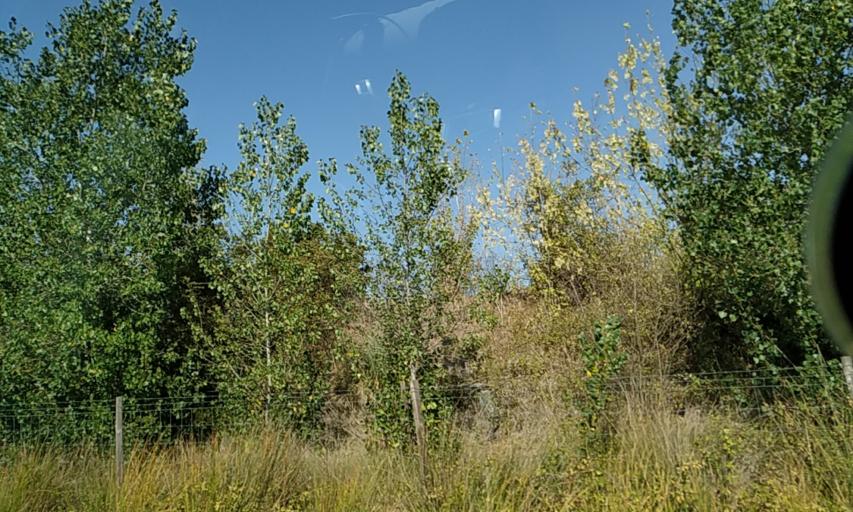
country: PT
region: Santarem
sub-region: Coruche
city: Coruche
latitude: 38.8010
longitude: -8.5789
